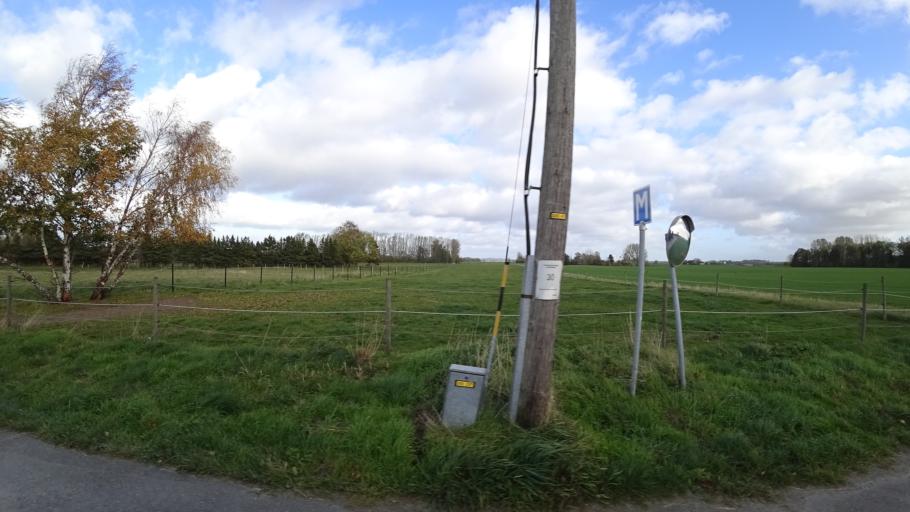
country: SE
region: Skane
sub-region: Staffanstorps Kommun
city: Staffanstorp
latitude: 55.6209
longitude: 13.2045
